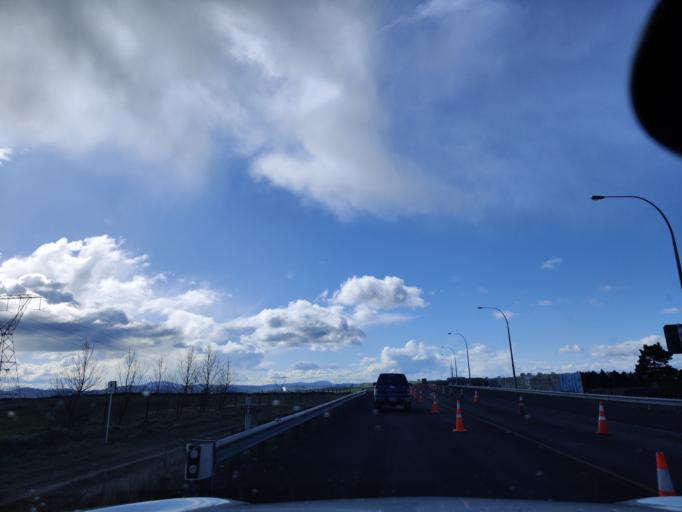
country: NZ
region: Waikato
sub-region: Taupo District
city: Taupo
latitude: -38.6876
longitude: 176.1138
